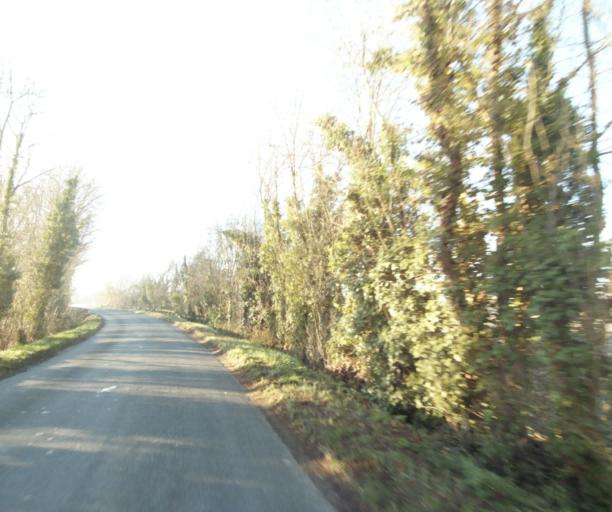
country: FR
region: Poitou-Charentes
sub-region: Departement de la Charente-Maritime
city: Cherac
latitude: 45.6802
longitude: -0.4626
